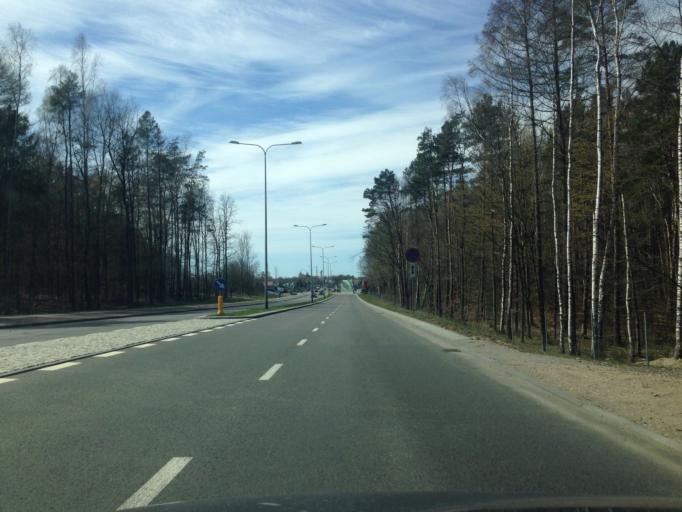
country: PL
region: Pomeranian Voivodeship
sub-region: Gdynia
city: Wielki Kack
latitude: 54.4997
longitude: 18.4768
